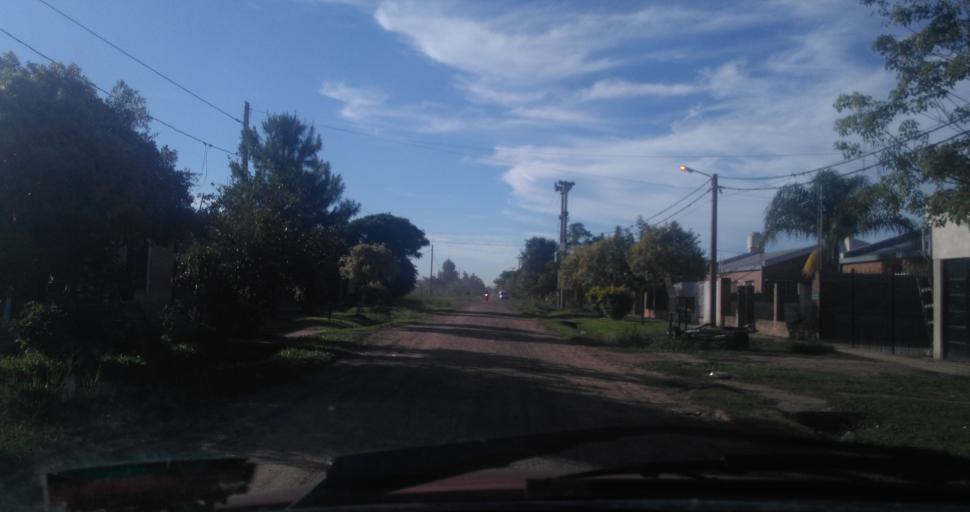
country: AR
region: Chaco
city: Fontana
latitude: -27.4138
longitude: -59.0248
